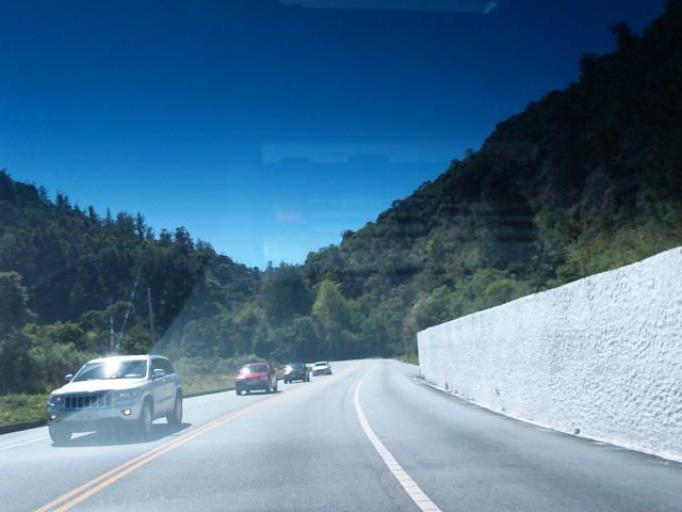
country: BR
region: Sao Paulo
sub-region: Campos Do Jordao
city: Campos do Jordao
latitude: -22.7788
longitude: -45.6106
